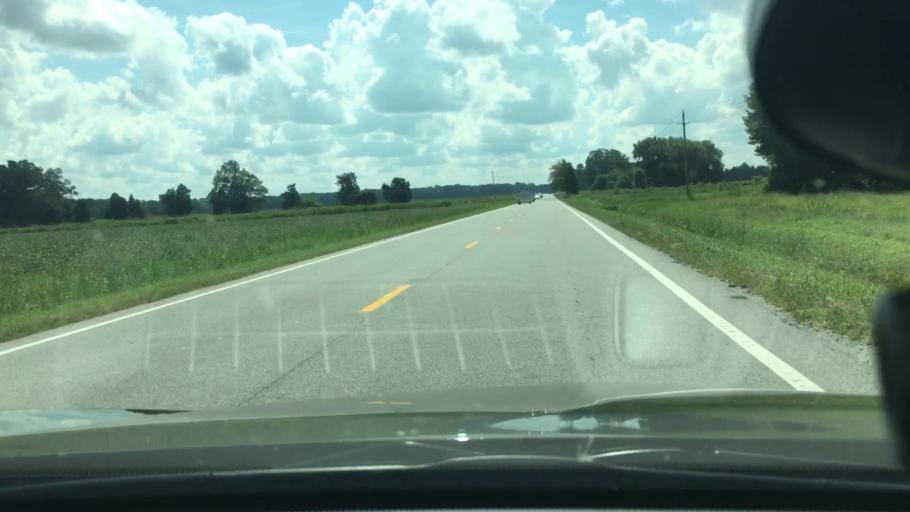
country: US
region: North Carolina
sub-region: Pitt County
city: Summerfield
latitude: 35.6637
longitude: -77.4755
